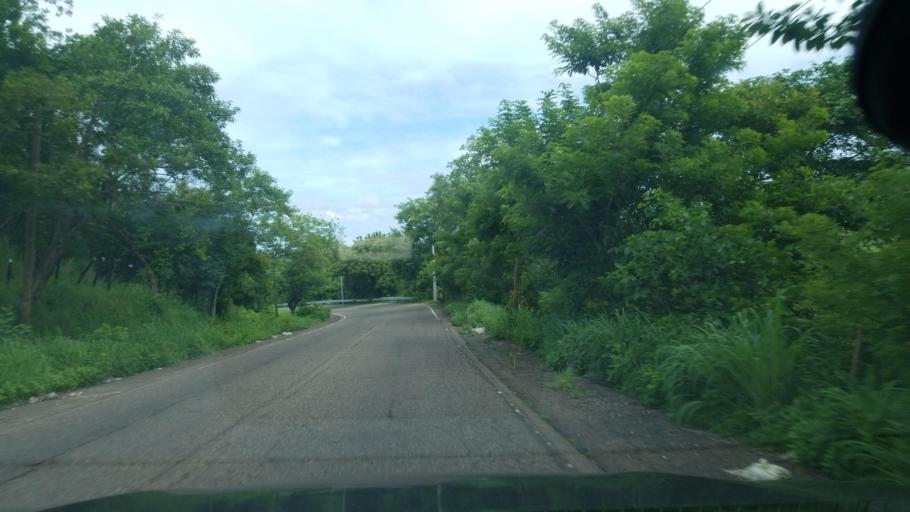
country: HN
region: Choluteca
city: Santa Ana de Yusguare
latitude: 13.3744
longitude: -87.0639
